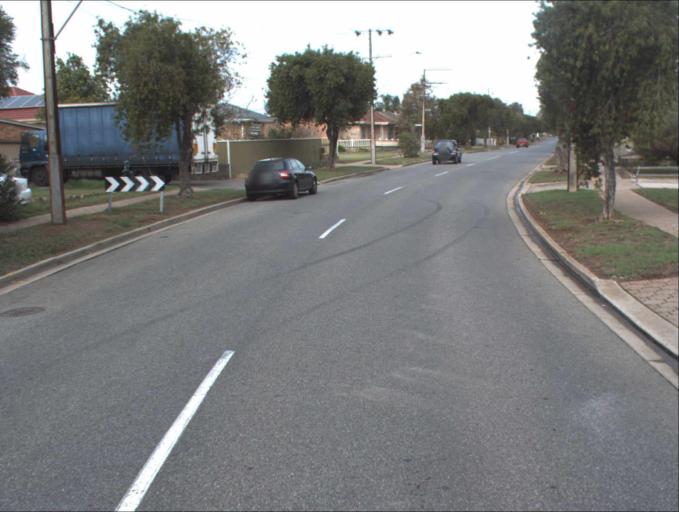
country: AU
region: South Australia
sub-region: Port Adelaide Enfield
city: Gilles Plains
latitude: -34.8407
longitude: 138.6547
